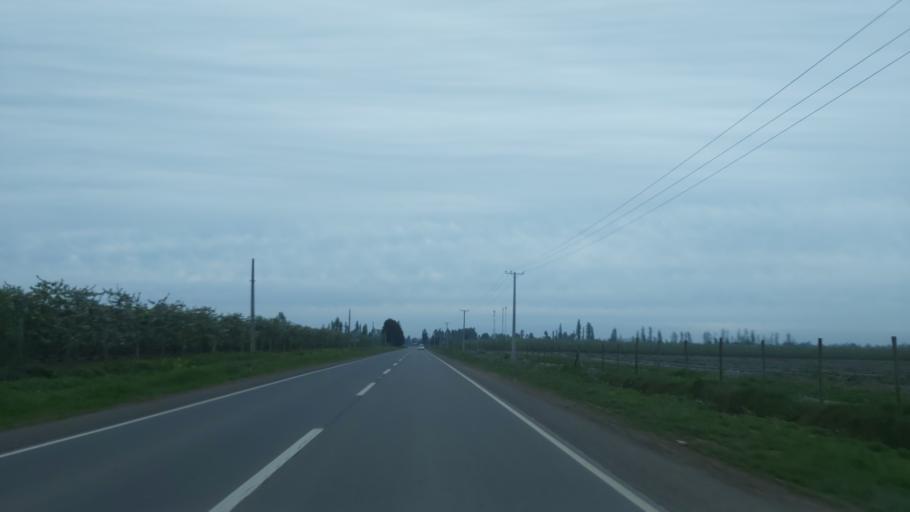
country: CL
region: Maule
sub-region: Provincia de Linares
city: Colbun
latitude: -35.7221
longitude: -71.4847
